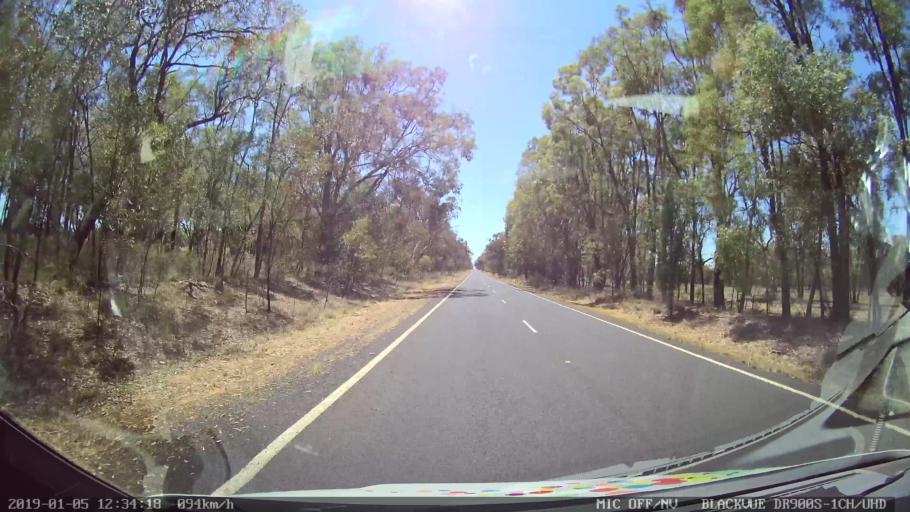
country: AU
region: New South Wales
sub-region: Warrumbungle Shire
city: Coonabarabran
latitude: -31.2125
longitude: 149.4081
